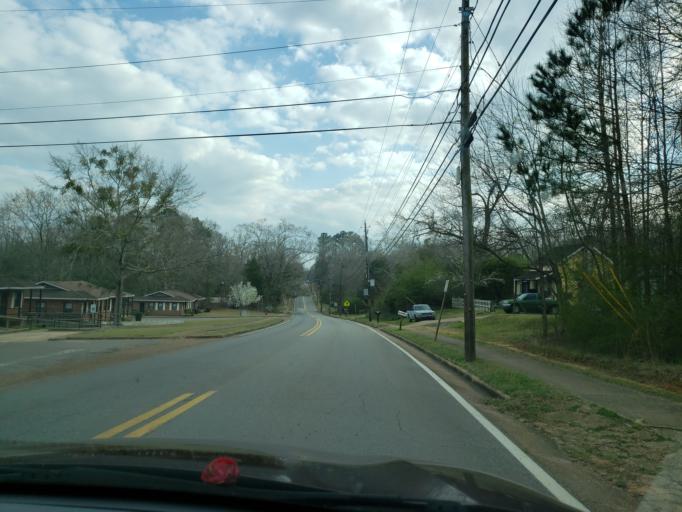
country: US
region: Alabama
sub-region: Hale County
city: Greensboro
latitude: 32.7101
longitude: -87.5921
